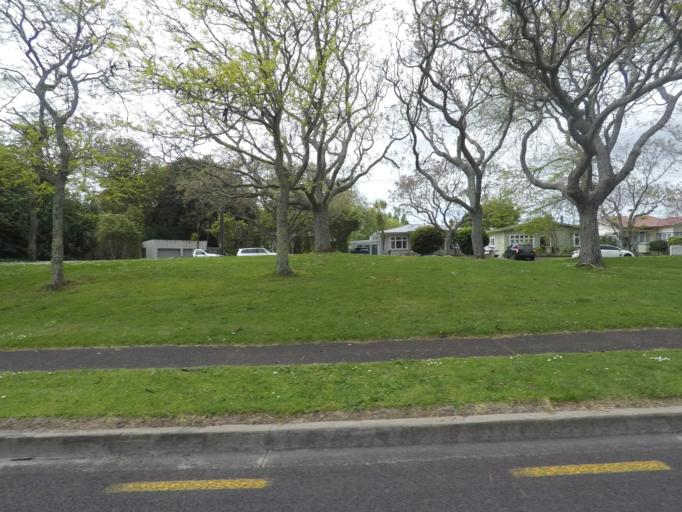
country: NZ
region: Auckland
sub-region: Auckland
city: Auckland
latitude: -36.8739
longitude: 174.7257
